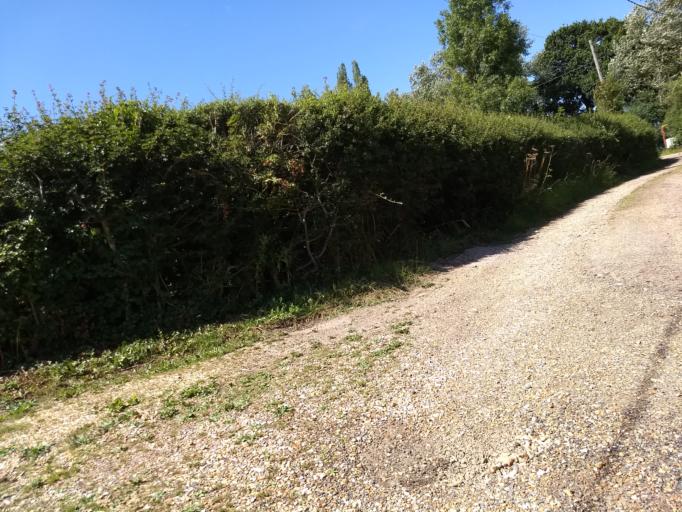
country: GB
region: England
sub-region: Isle of Wight
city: Ryde
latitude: 50.7064
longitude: -1.1624
